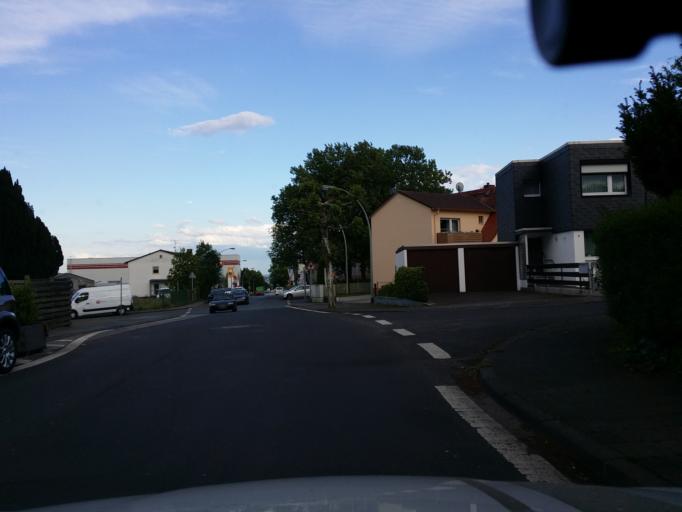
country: DE
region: Hesse
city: Kelkheim (Taunus)
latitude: 50.1233
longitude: 8.4620
